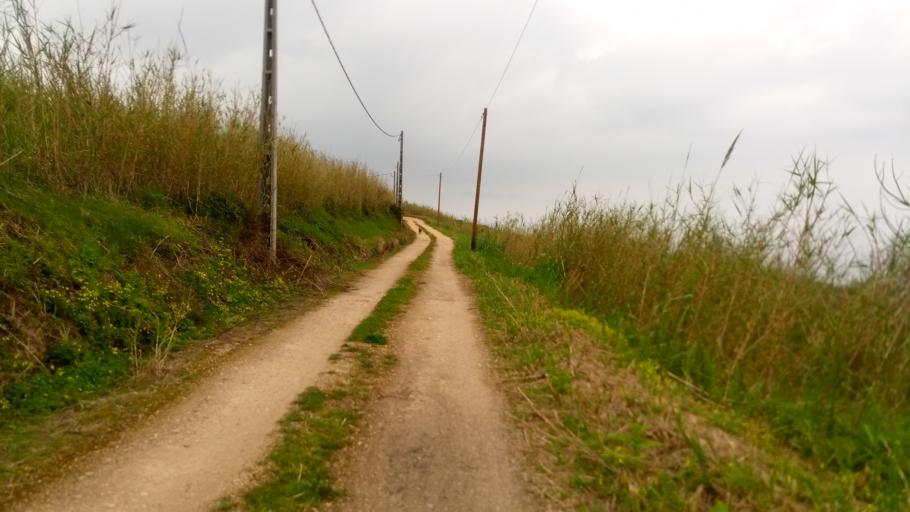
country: PT
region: Leiria
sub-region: Caldas da Rainha
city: Caldas da Rainha
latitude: 39.4720
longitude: -9.1956
